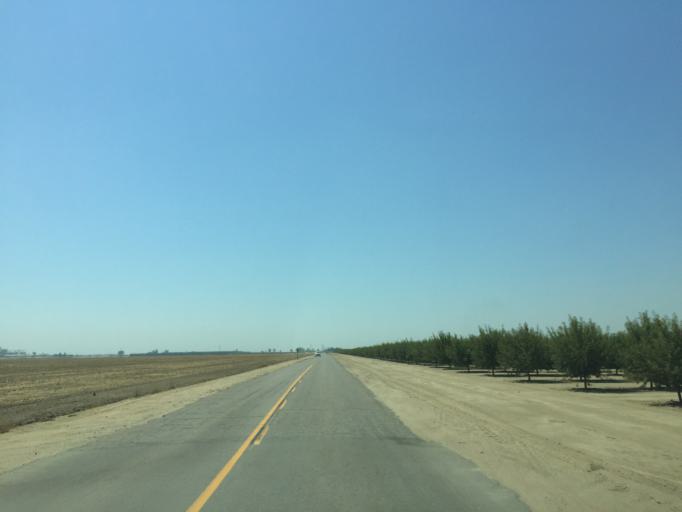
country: US
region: California
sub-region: Tulare County
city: Goshen
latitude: 36.3709
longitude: -119.3949
